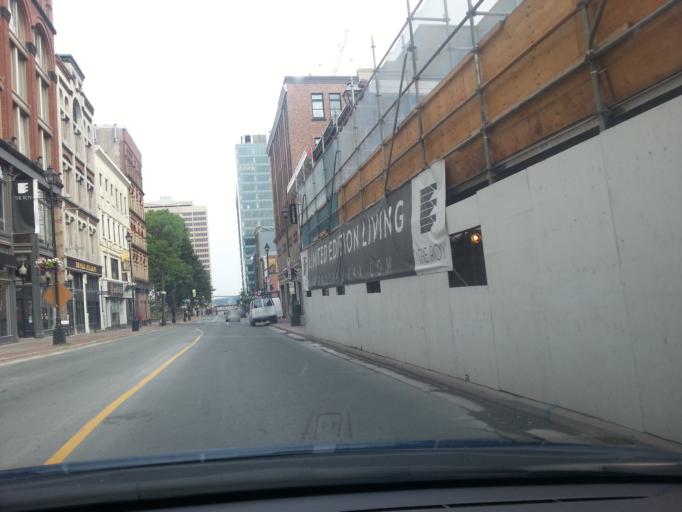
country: CA
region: Nova Scotia
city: Halifax
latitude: 44.6465
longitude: -63.5737
